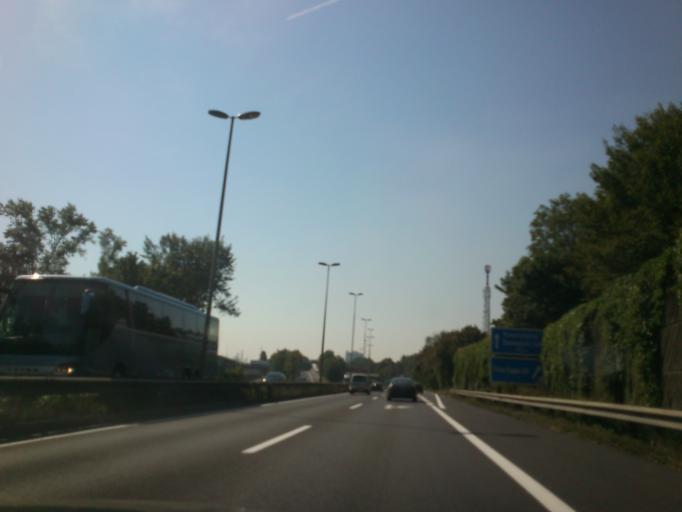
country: AT
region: Upper Austria
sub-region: Linz Stadt
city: Linz
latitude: 48.3046
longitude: 14.3135
